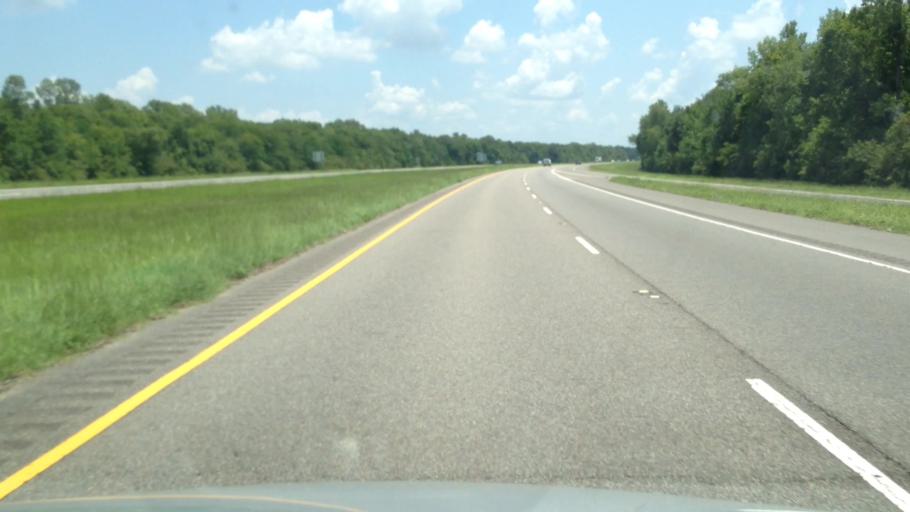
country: US
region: Louisiana
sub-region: Avoyelles Parish
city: Bunkie
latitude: 30.9857
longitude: -92.3052
